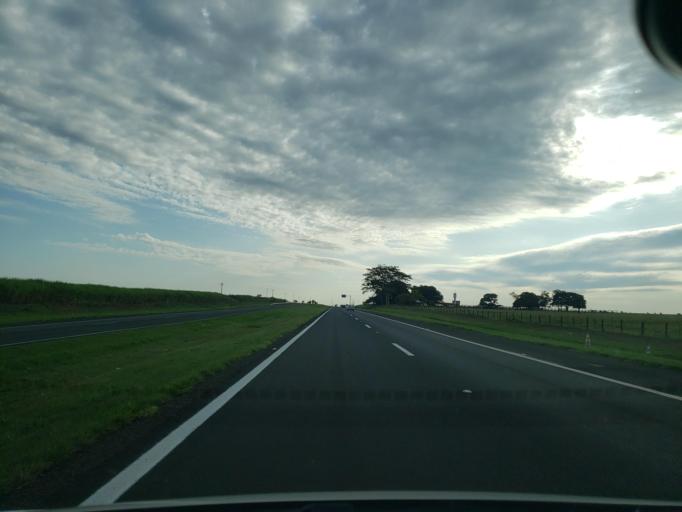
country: BR
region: Sao Paulo
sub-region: Guararapes
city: Guararapes
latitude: -21.2129
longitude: -50.7091
